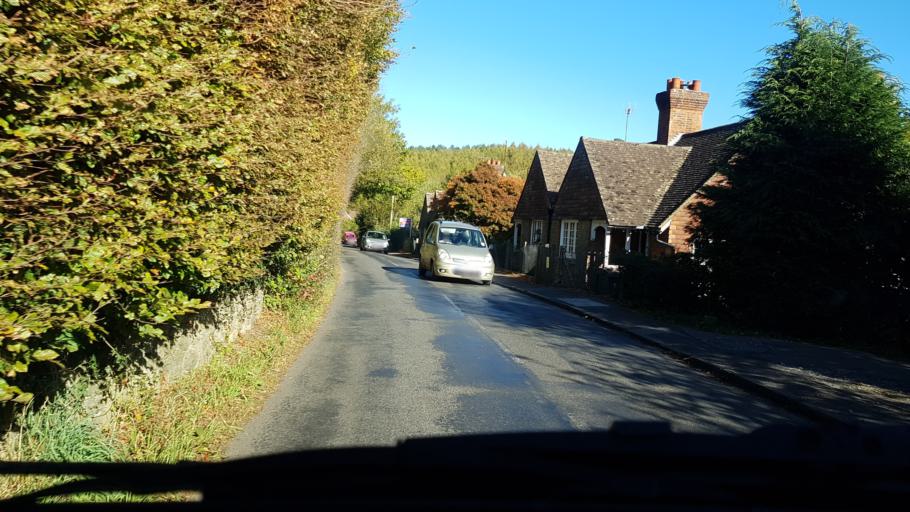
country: GB
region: England
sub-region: Surrey
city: Ockley
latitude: 51.1908
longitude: -0.4117
